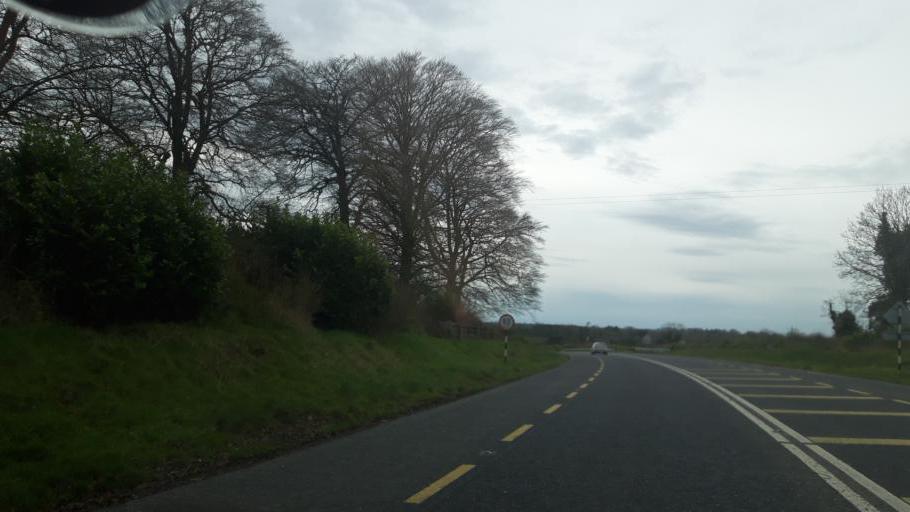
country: IE
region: Leinster
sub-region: Kildare
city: Derrinturn
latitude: 53.3527
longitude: -6.9659
